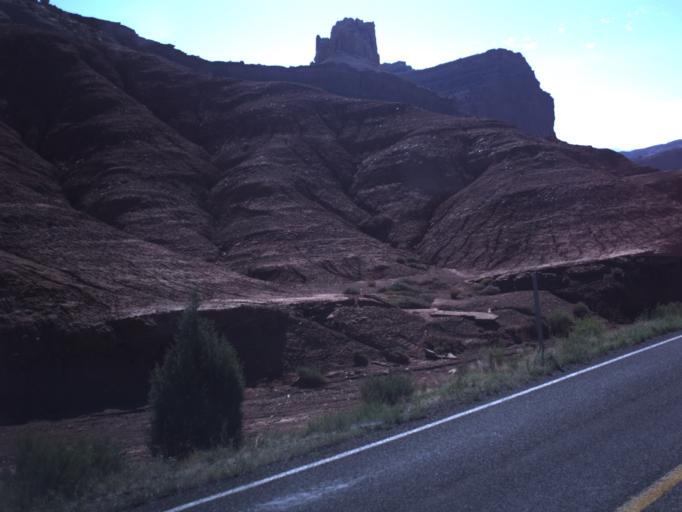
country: US
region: Utah
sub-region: Wayne County
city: Loa
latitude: 38.3013
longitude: -111.2755
